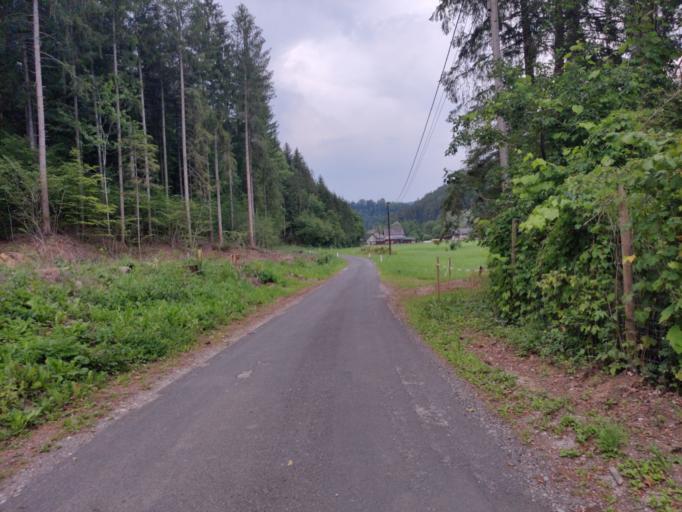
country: AT
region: Styria
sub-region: Politischer Bezirk Graz-Umgebung
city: Gratwein
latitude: 47.1145
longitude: 15.2962
